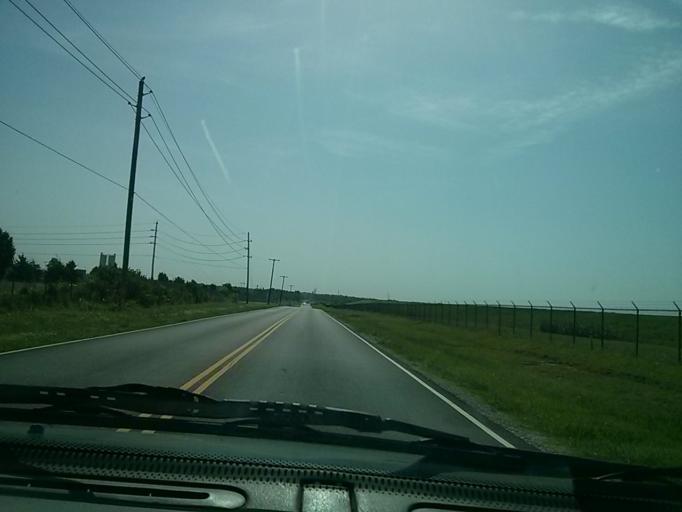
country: US
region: Oklahoma
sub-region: Rogers County
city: Catoosa
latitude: 36.1335
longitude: -95.7719
